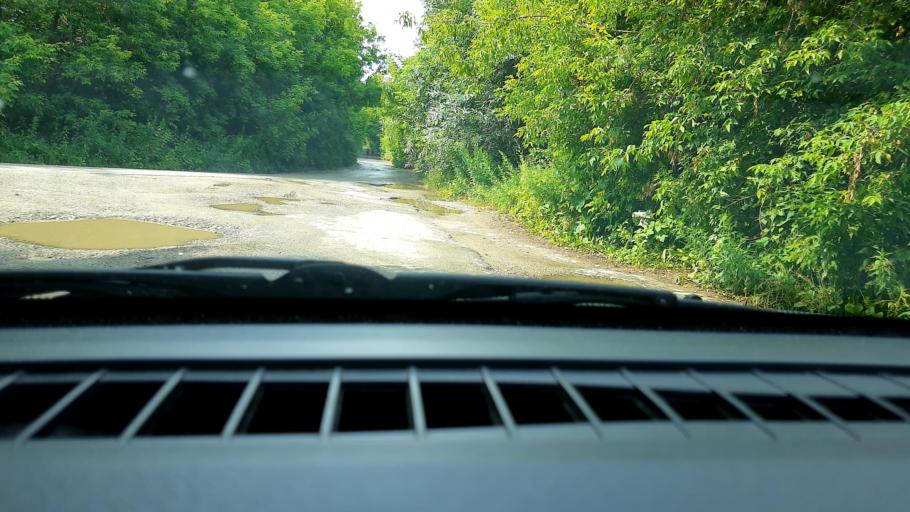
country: RU
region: Nizjnij Novgorod
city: Neklyudovo
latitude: 56.3956
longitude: 43.8485
